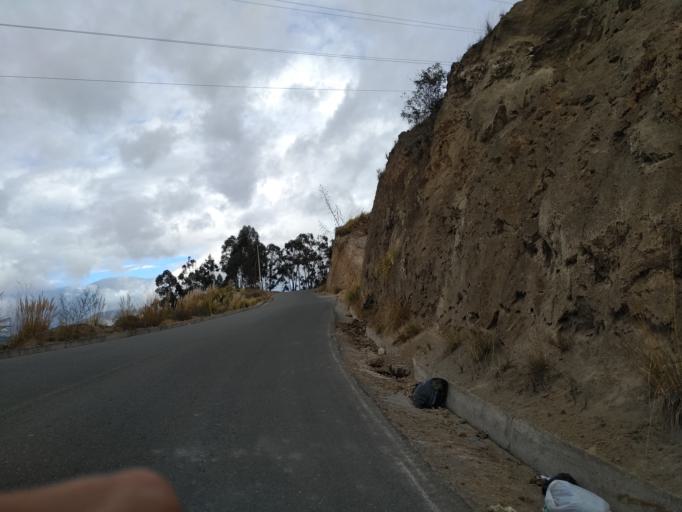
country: EC
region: Chimborazo
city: Riobamba
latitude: -1.6852
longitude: -78.6835
